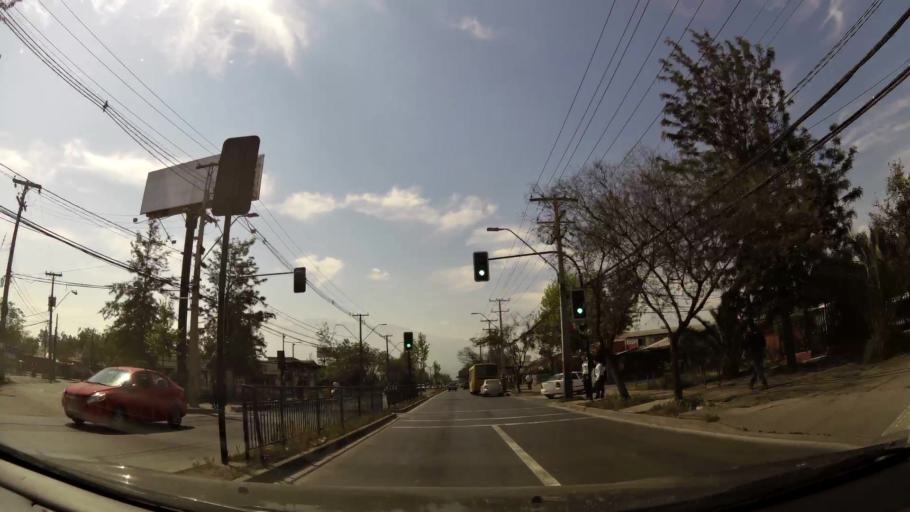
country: CL
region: Santiago Metropolitan
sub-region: Provincia de Cordillera
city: Puente Alto
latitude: -33.5804
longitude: -70.5900
